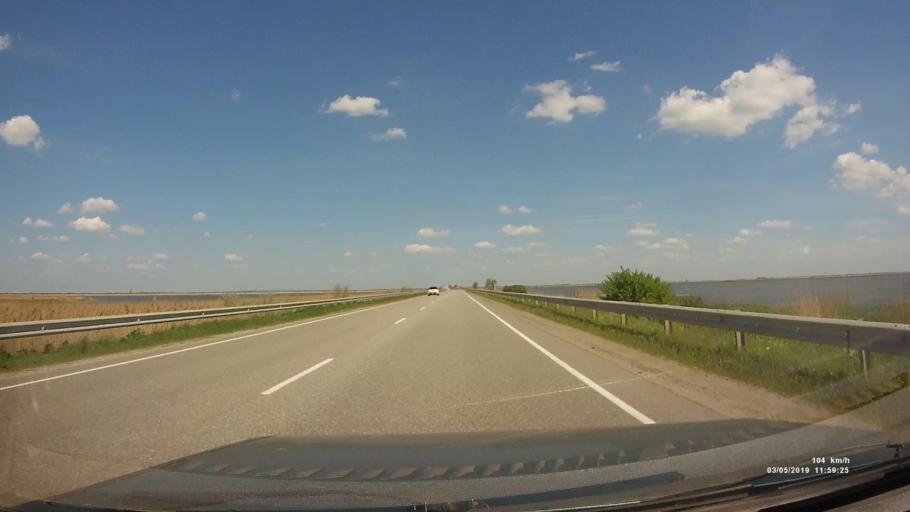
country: RU
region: Rostov
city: Bagayevskaya
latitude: 47.2347
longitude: 40.3302
